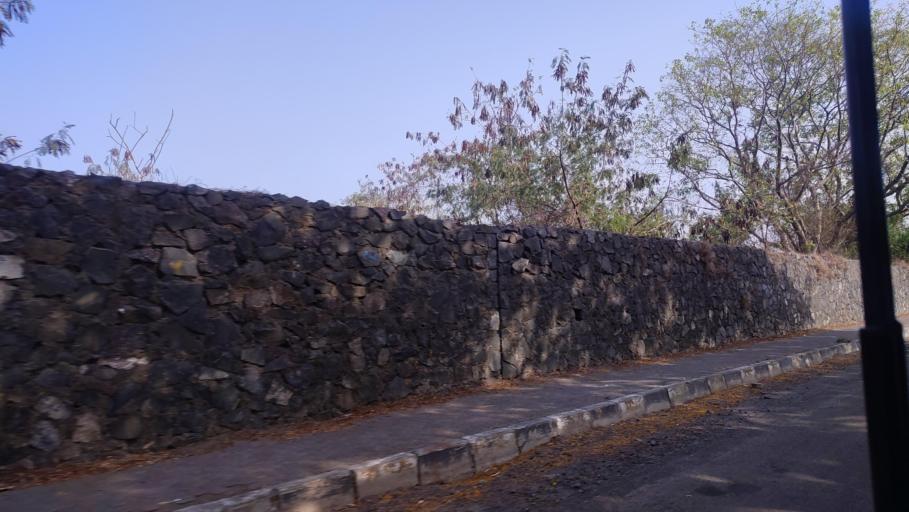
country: IN
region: Maharashtra
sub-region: Mumbai Suburban
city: Powai
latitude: 19.1017
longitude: 72.9296
